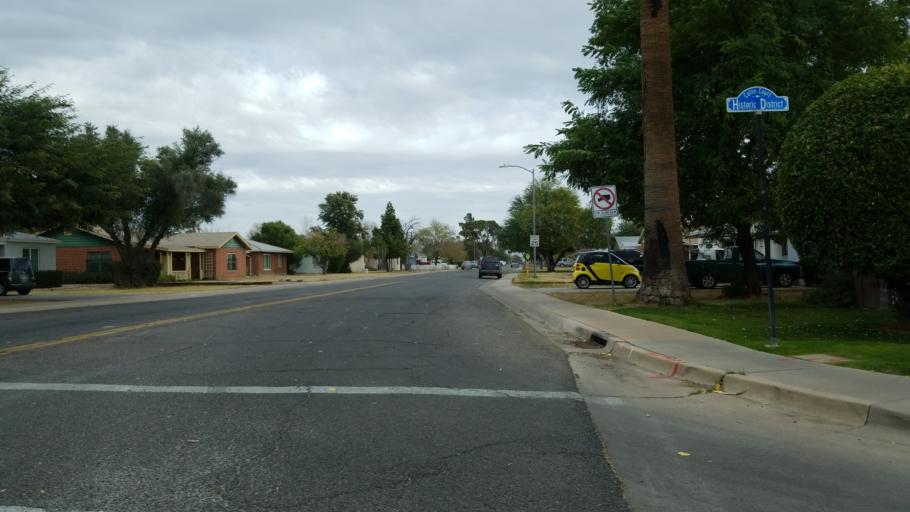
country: US
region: Arizona
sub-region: Maricopa County
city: Glendale
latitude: 33.5457
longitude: -112.1861
